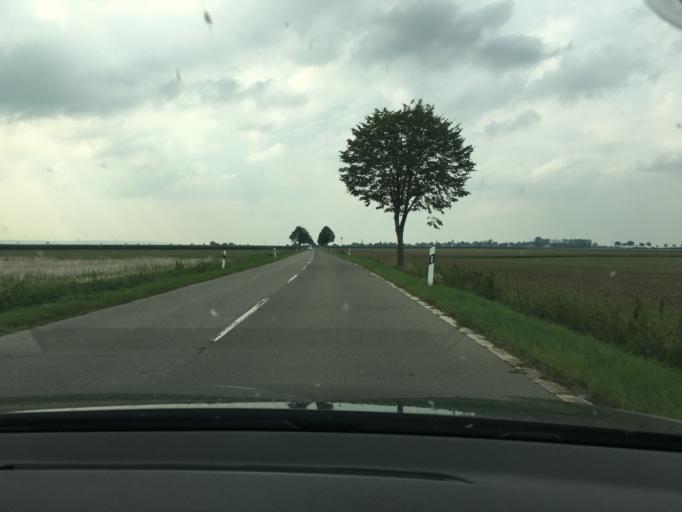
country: DE
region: North Rhine-Westphalia
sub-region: Regierungsbezirk Koln
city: Norvenich
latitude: 50.7903
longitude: 6.5938
